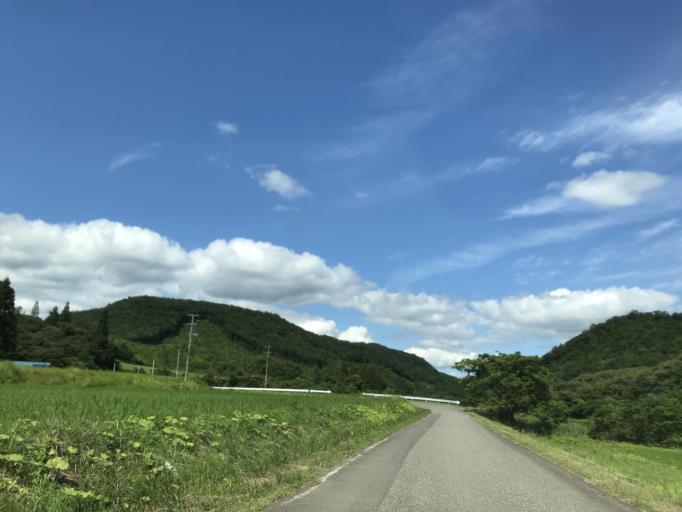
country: JP
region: Iwate
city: Ichinoseki
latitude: 38.9293
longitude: 140.9558
